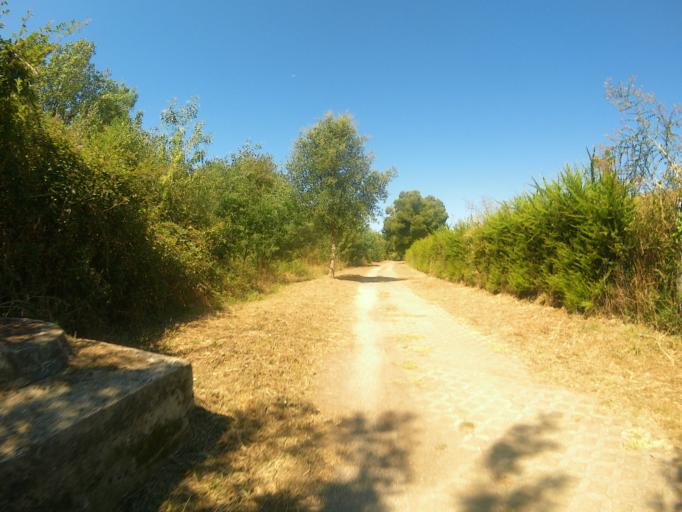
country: PT
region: Viana do Castelo
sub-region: Ponte de Lima
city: Ponte de Lima
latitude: 41.7630
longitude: -8.5979
